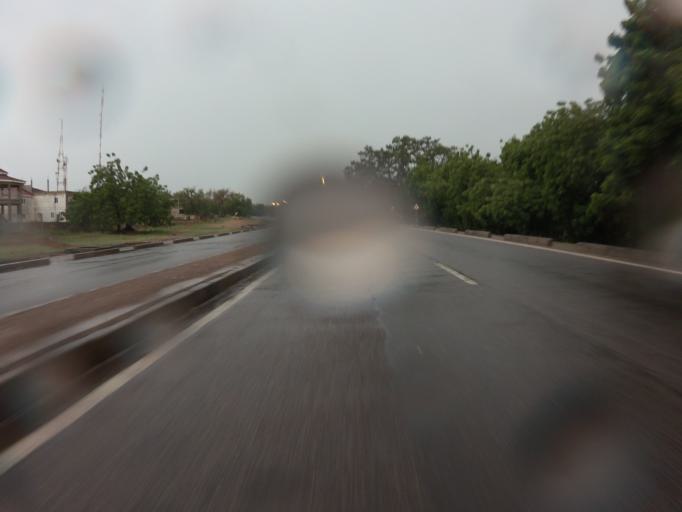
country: GH
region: Upper East
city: Bolgatanga
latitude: 10.7999
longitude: -0.8605
